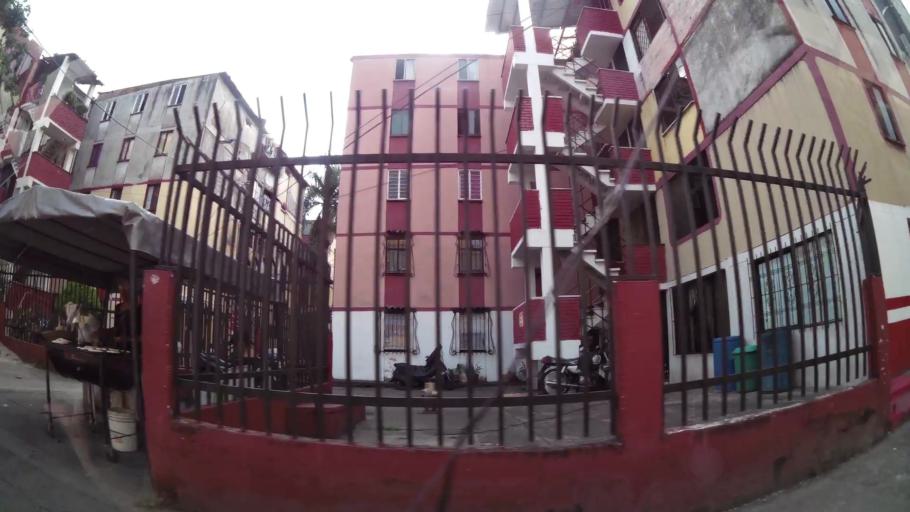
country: CO
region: Valle del Cauca
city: Cali
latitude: 3.4765
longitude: -76.4899
